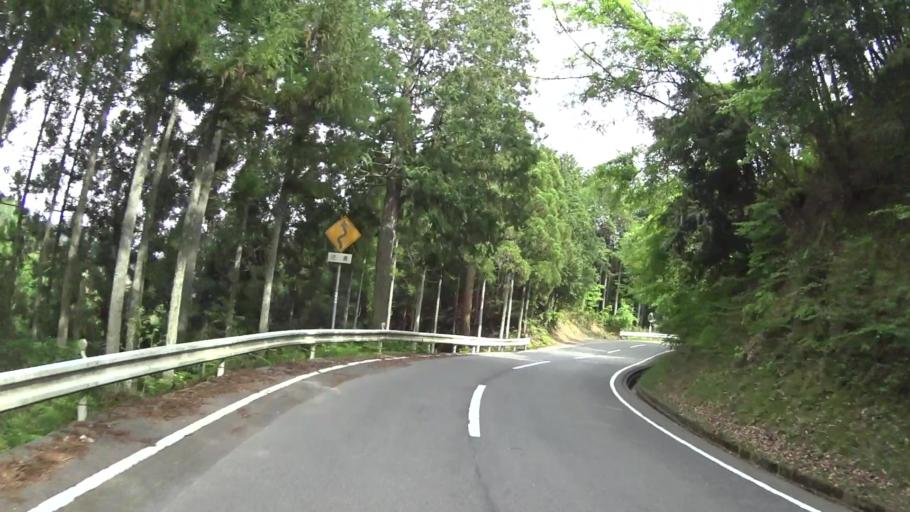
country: JP
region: Kyoto
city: Kameoka
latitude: 35.1521
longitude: 135.6270
